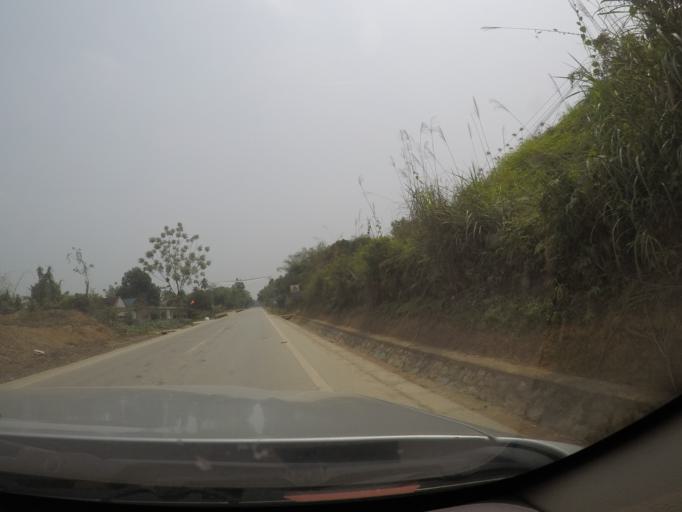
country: VN
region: Thanh Hoa
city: Thi Tran Yen Cat
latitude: 19.7120
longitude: 105.4365
